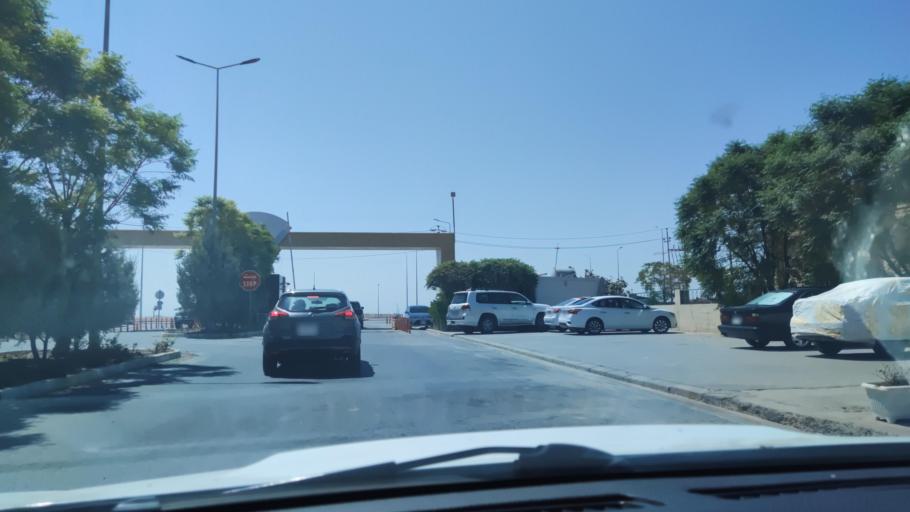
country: IQ
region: Arbil
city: Erbil
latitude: 36.2868
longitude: 44.0494
